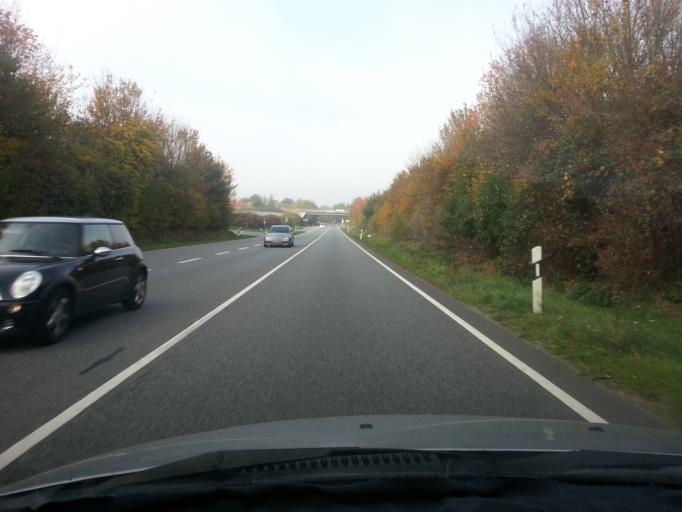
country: DE
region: Hesse
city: Langen
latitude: 49.9979
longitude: 8.6733
